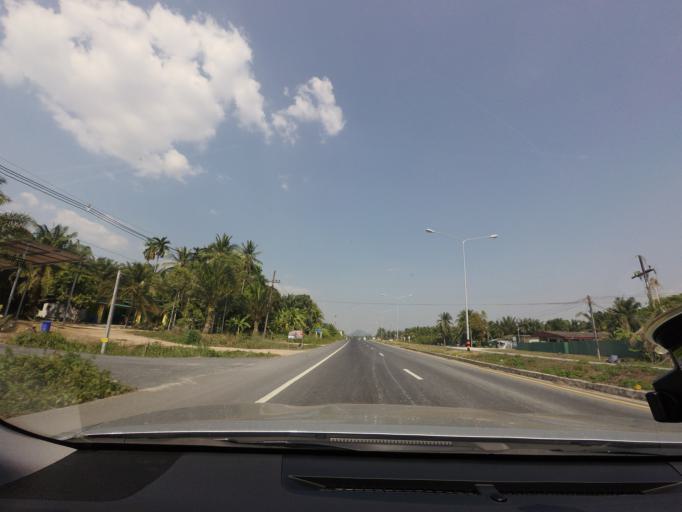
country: TH
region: Phangnga
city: Thap Put
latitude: 8.5390
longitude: 98.7167
